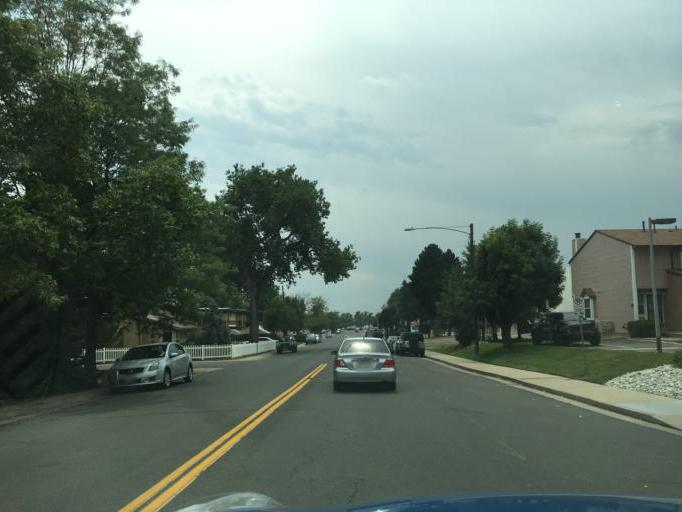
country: US
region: Colorado
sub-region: Jefferson County
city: Wheat Ridge
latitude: 39.7439
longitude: -105.0908
